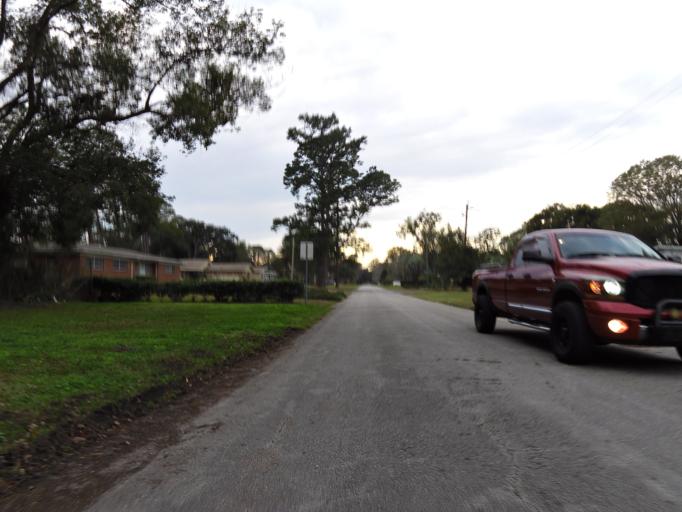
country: US
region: Florida
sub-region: Duval County
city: Jacksonville
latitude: 30.2421
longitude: -81.6169
